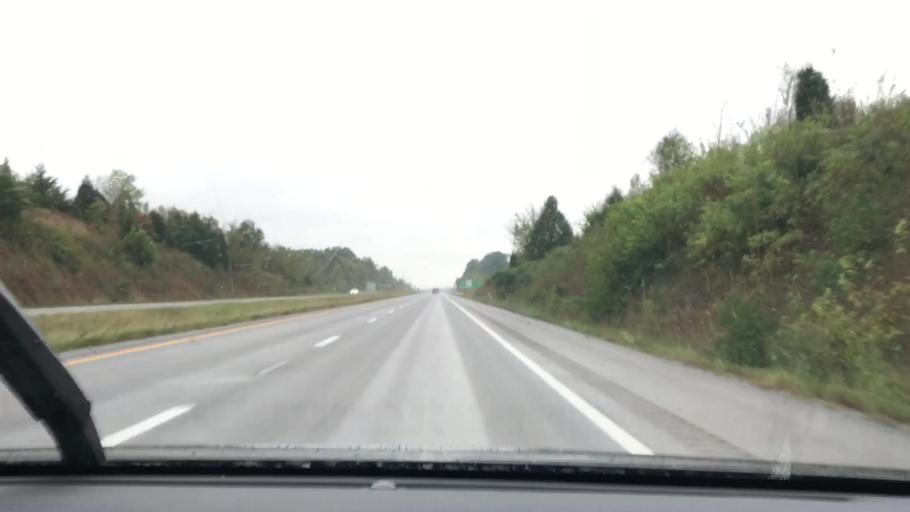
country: US
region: Kentucky
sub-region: Hopkins County
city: Nortonville
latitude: 37.1823
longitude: -87.4455
